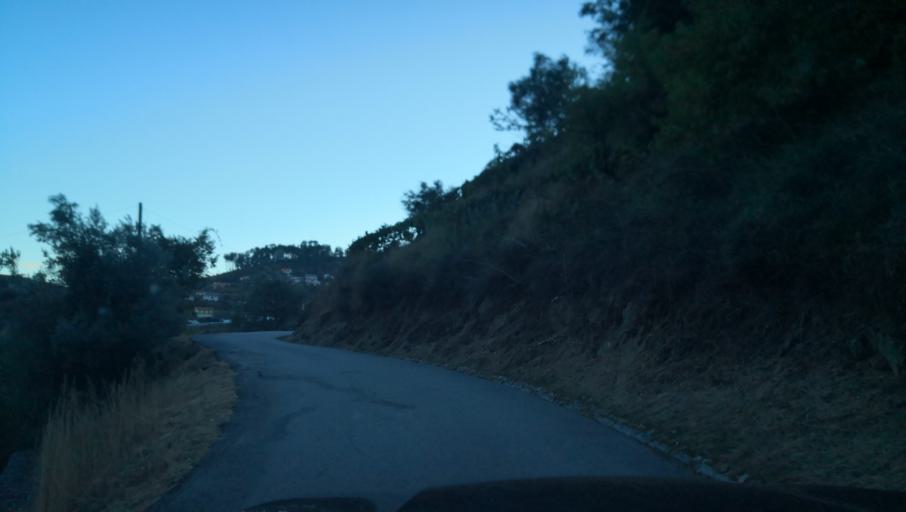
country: PT
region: Vila Real
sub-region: Santa Marta de Penaguiao
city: Santa Marta de Penaguiao
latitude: 41.2590
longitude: -7.8198
